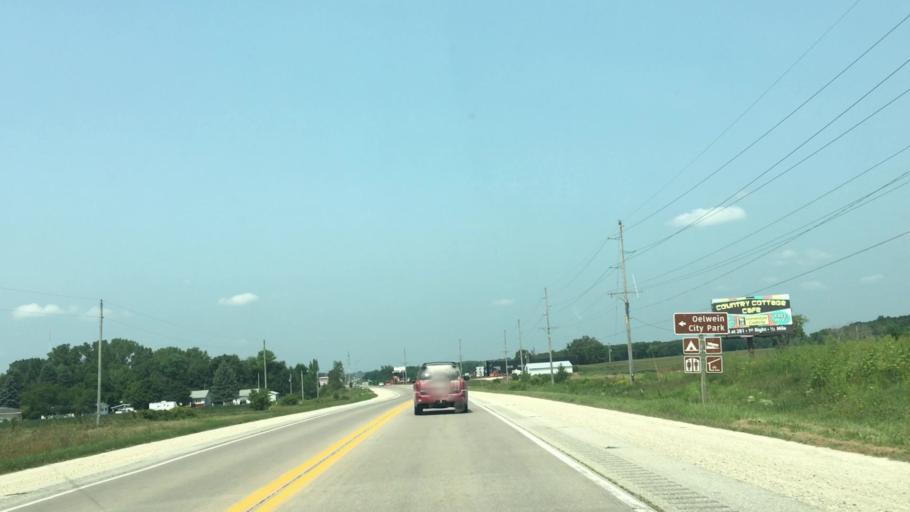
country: US
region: Iowa
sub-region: Fayette County
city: Oelwein
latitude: 42.6385
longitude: -91.9086
